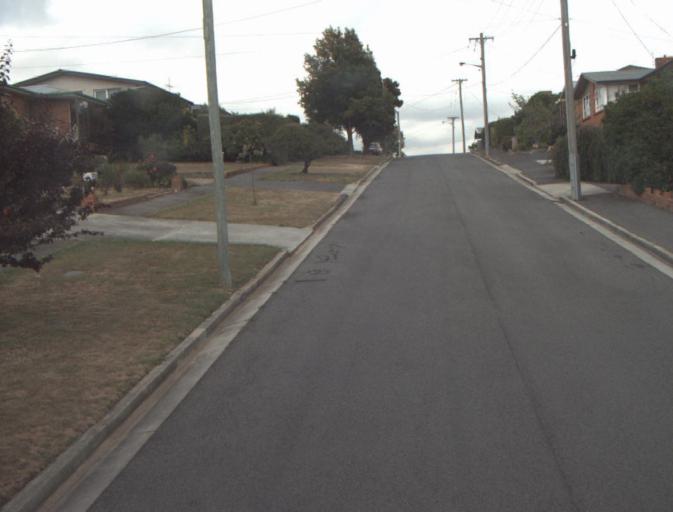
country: AU
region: Tasmania
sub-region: Launceston
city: Summerhill
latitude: -41.4807
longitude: 147.1626
